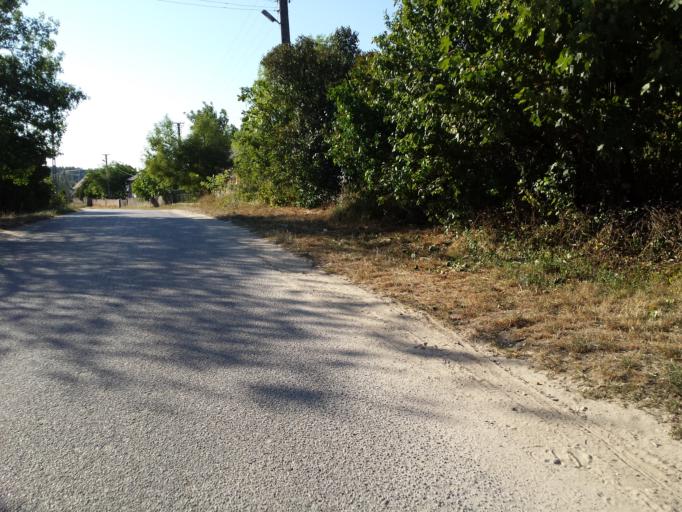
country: PL
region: Swietokrzyskie
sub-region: Powiat kielecki
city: Pierzchnica
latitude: 50.6561
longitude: 20.7963
